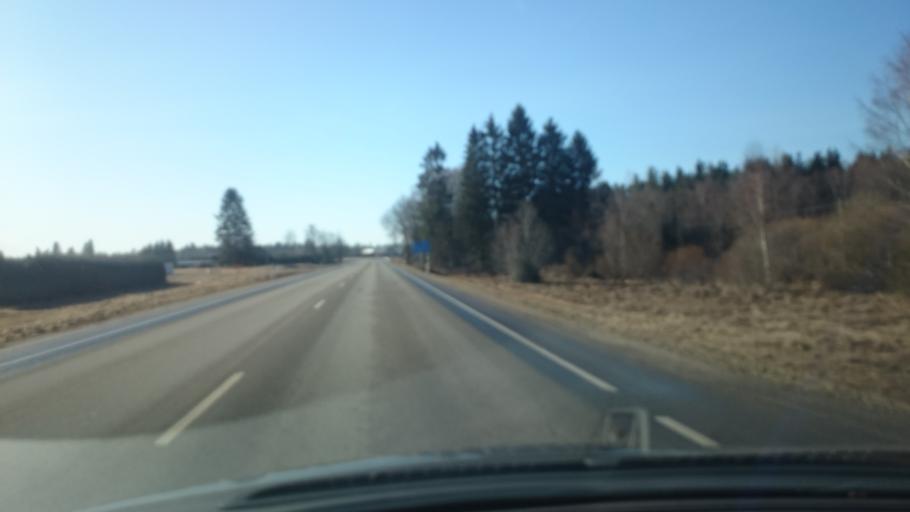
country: EE
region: Raplamaa
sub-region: Kohila vald
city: Kohila
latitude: 59.2550
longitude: 24.7412
